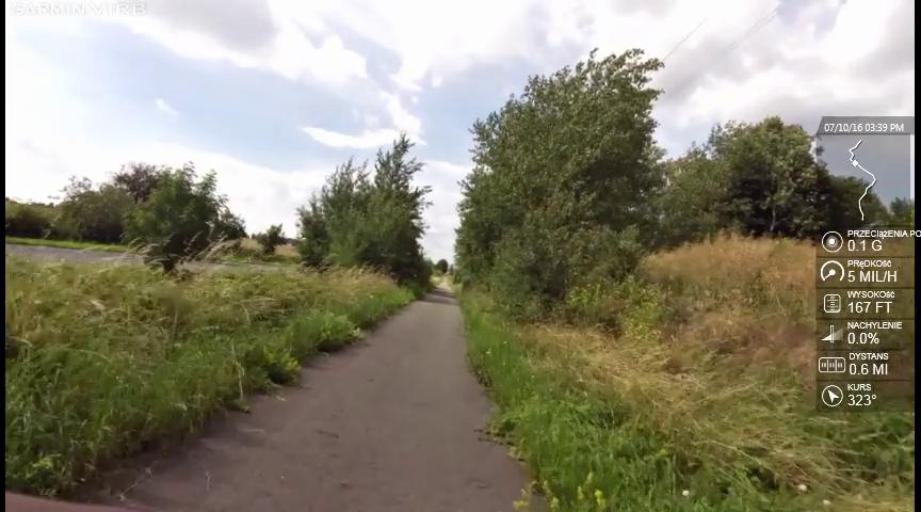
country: PL
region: West Pomeranian Voivodeship
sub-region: Powiat gryfinski
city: Banie
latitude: 53.1208
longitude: 14.6207
